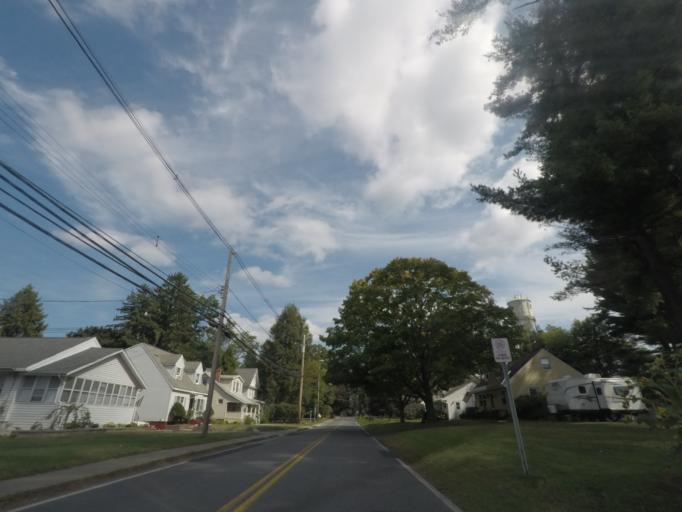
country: US
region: New York
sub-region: Albany County
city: Delmar
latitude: 42.6213
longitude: -73.8251
